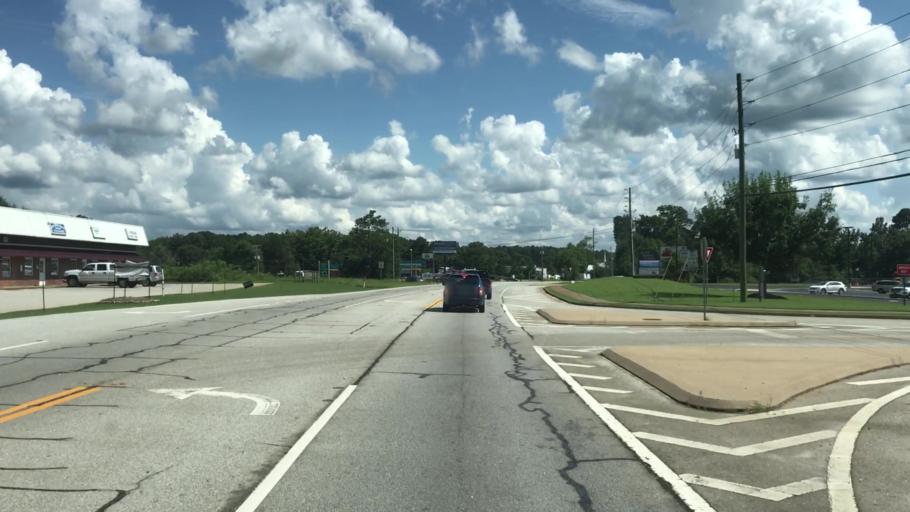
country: US
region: Georgia
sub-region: Walton County
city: Walnut Grove
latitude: 33.7806
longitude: -83.8533
